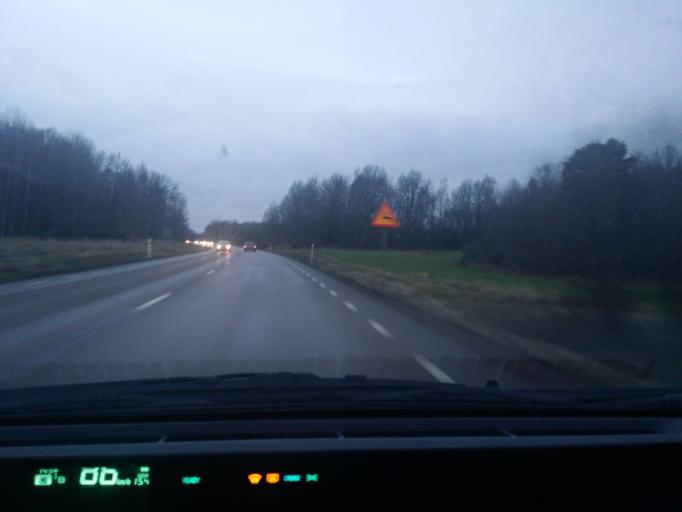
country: SE
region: Soedermanland
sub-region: Eskilstuna Kommun
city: Kvicksund
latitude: 59.4667
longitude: 16.3139
